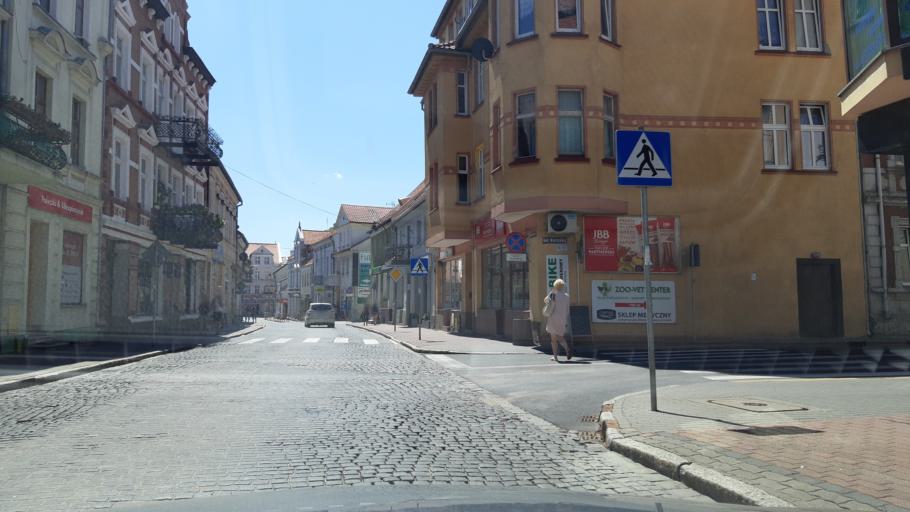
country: PL
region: Warmian-Masurian Voivodeship
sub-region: Powiat mragowski
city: Mragowo
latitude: 53.8727
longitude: 21.3039
